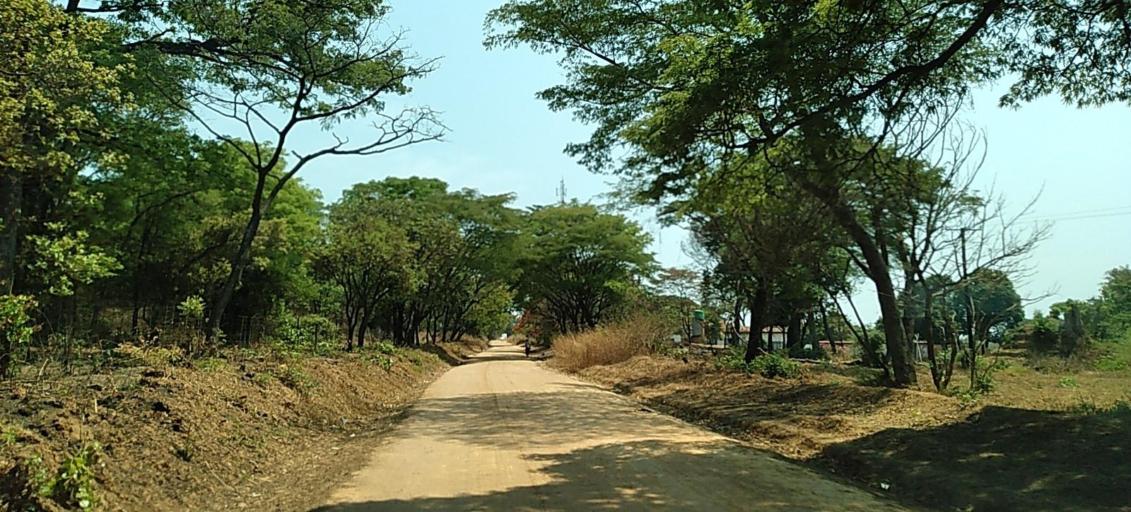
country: ZM
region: Copperbelt
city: Chingola
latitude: -12.6015
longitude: 27.9552
